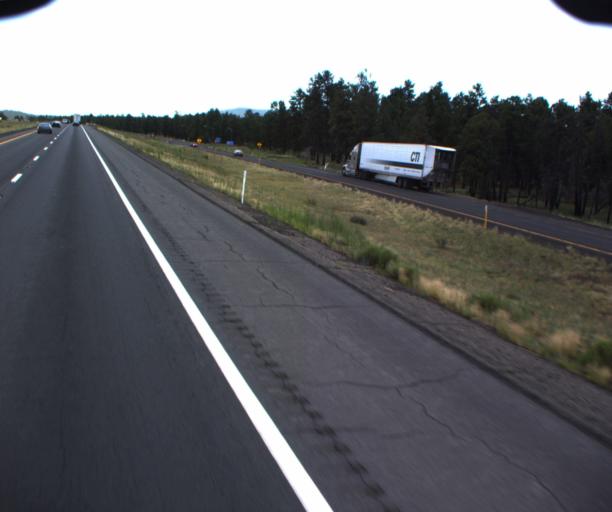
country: US
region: Arizona
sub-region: Coconino County
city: Williams
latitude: 35.2616
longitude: -112.1545
